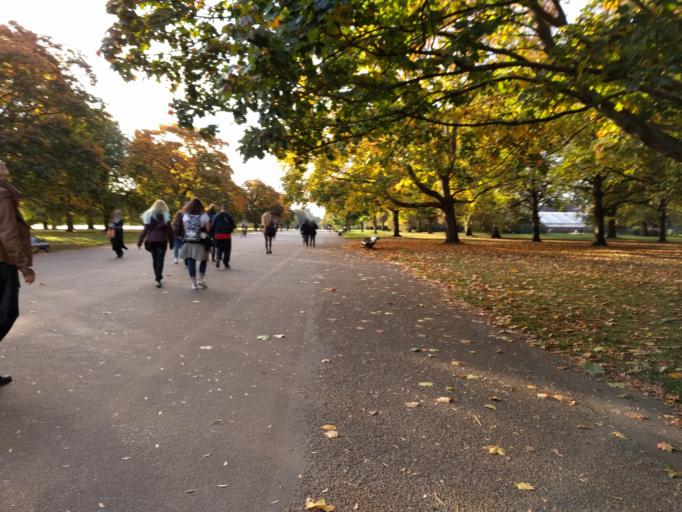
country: GB
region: England
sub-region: Greater London
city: Bayswater
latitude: 51.5079
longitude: -0.1869
